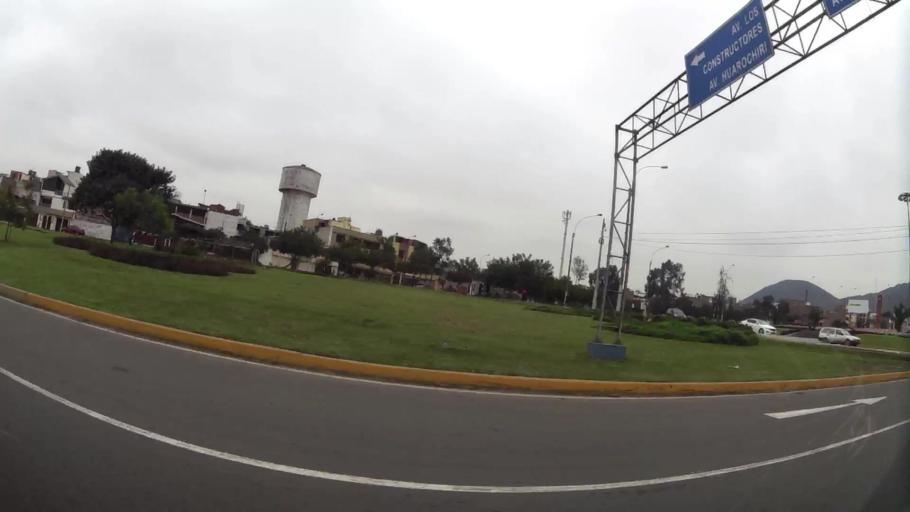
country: PE
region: Lima
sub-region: Lima
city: La Molina
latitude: -12.0651
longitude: -76.9406
